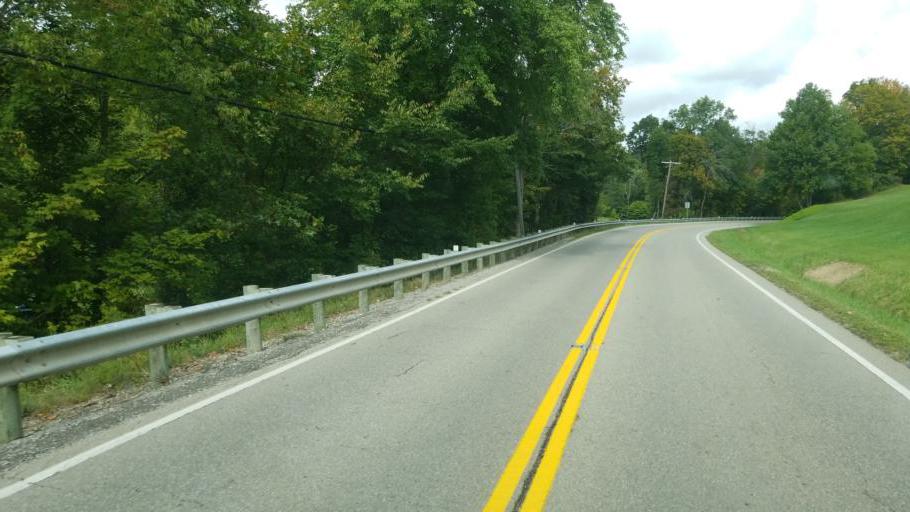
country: US
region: Ohio
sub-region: Jackson County
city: Oak Hill
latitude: 38.8959
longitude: -82.5914
